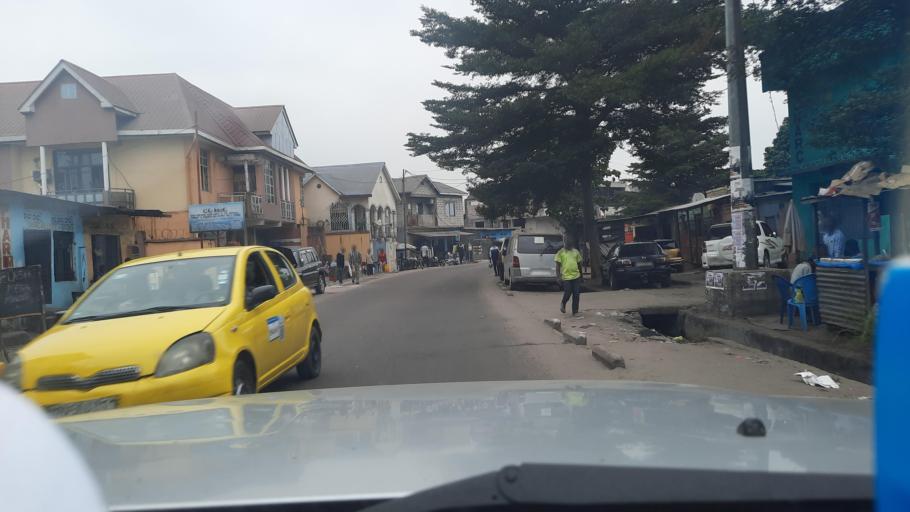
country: CD
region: Kinshasa
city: Masina
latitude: -4.3811
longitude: 15.3467
